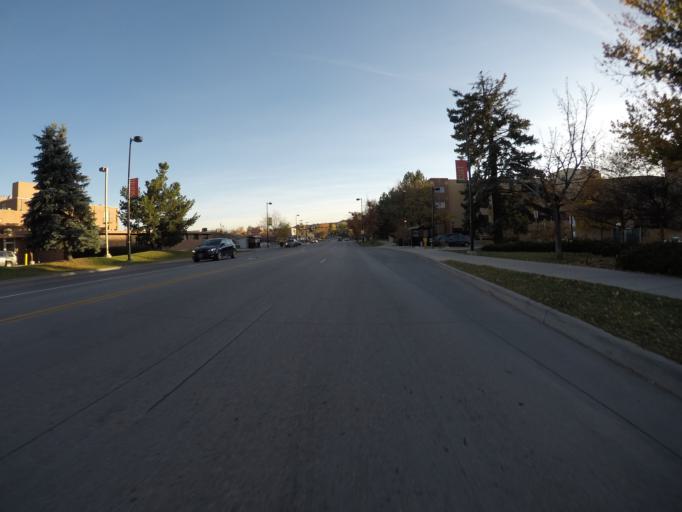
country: US
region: Colorado
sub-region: Boulder County
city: Boulder
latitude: 40.0266
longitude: -105.2821
